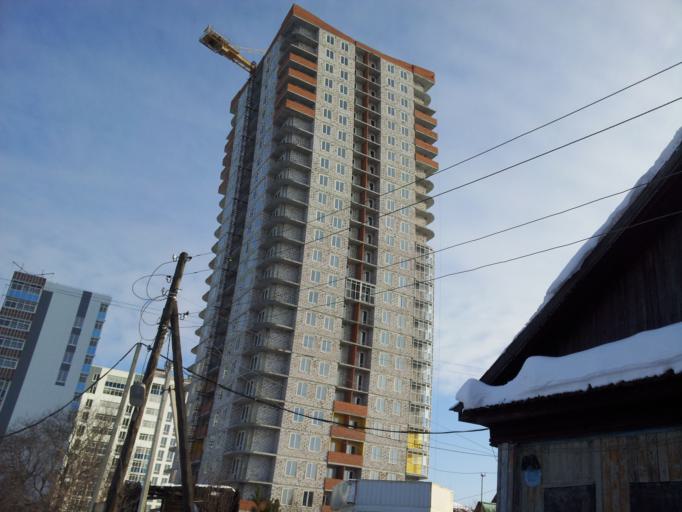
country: RU
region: Perm
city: Perm
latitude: 58.0212
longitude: 56.2628
